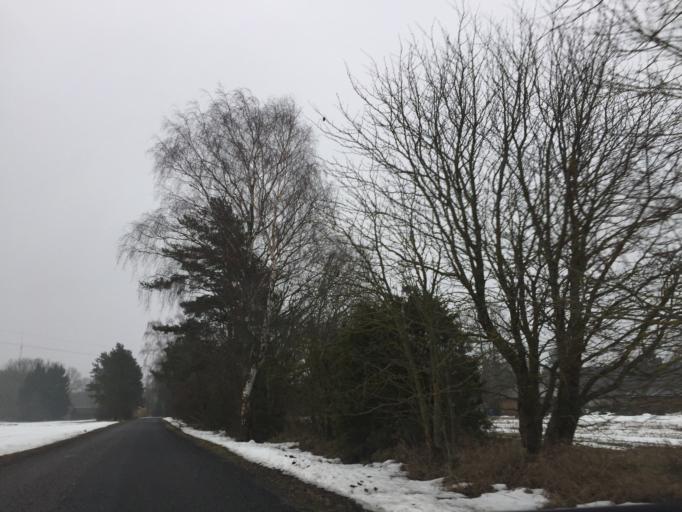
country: EE
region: Saare
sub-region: Kuressaare linn
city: Kuressaare
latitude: 58.2719
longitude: 22.5792
